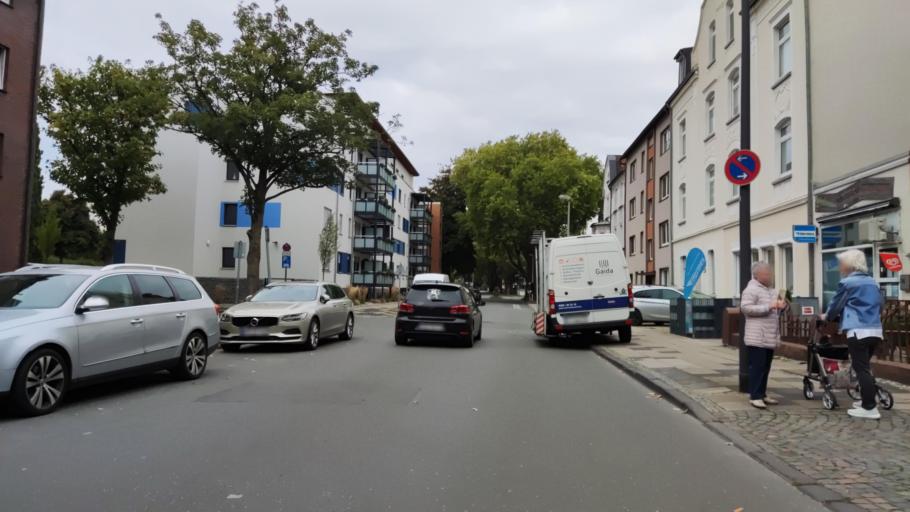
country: DE
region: North Rhine-Westphalia
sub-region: Regierungsbezirk Arnsberg
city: Herne
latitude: 51.5465
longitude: 7.2050
